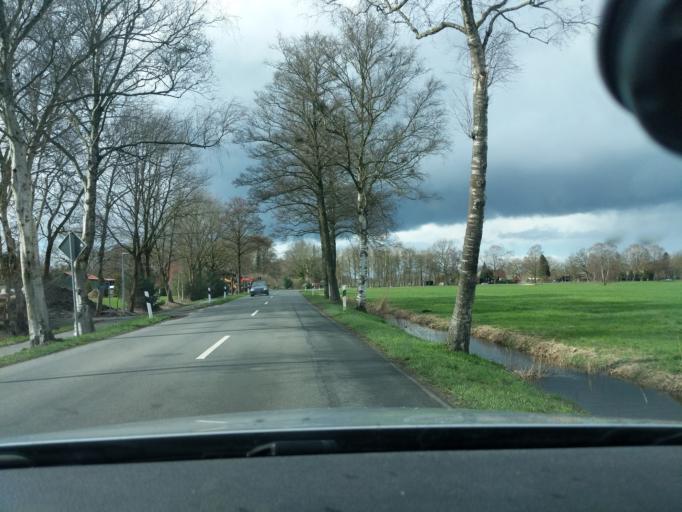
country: DE
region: Lower Saxony
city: Stade
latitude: 53.6257
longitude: 9.4350
